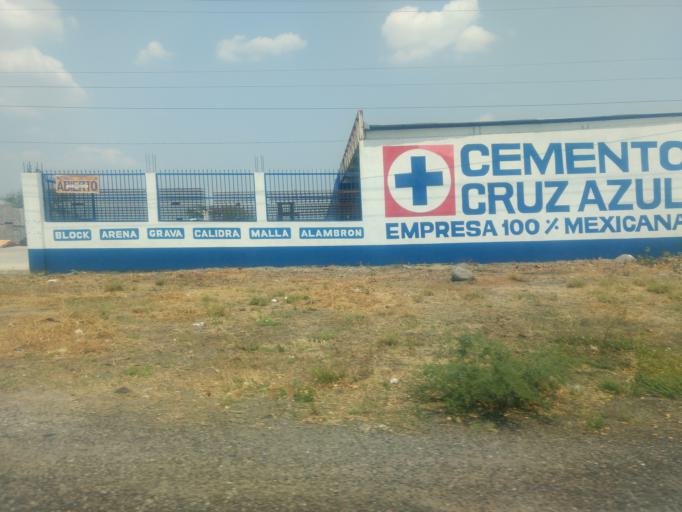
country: MX
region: Morelos
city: Xoxocotla
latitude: 18.7051
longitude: -99.2761
